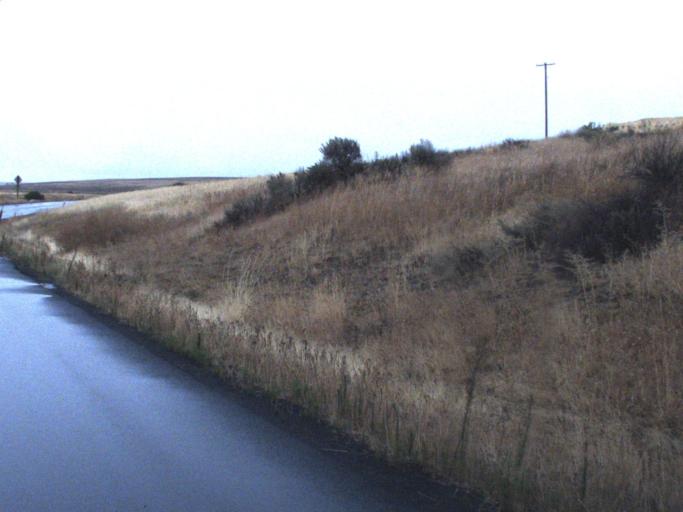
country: US
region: Washington
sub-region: Lincoln County
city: Davenport
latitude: 47.3879
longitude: -118.1435
